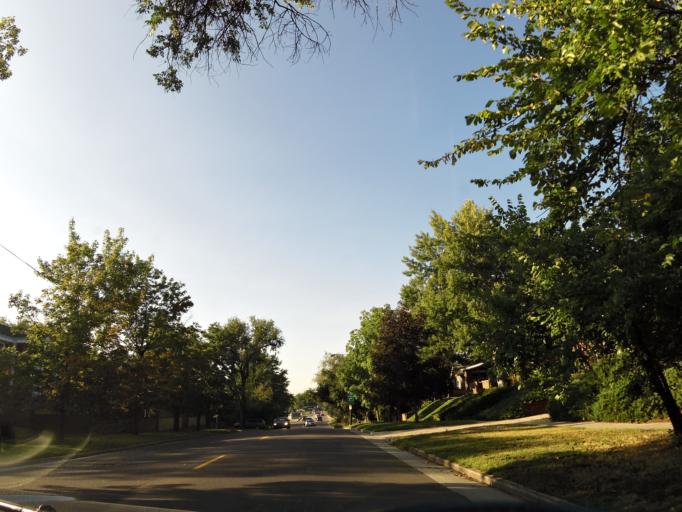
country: US
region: Colorado
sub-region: Arapahoe County
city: Glendale
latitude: 39.6923
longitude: -104.9735
